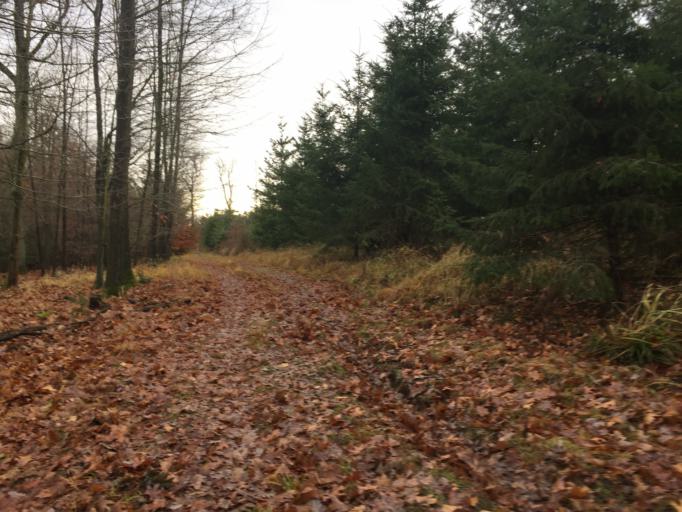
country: DE
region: Hesse
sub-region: Regierungsbezirk Giessen
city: Lich
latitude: 50.5357
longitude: 8.7926
